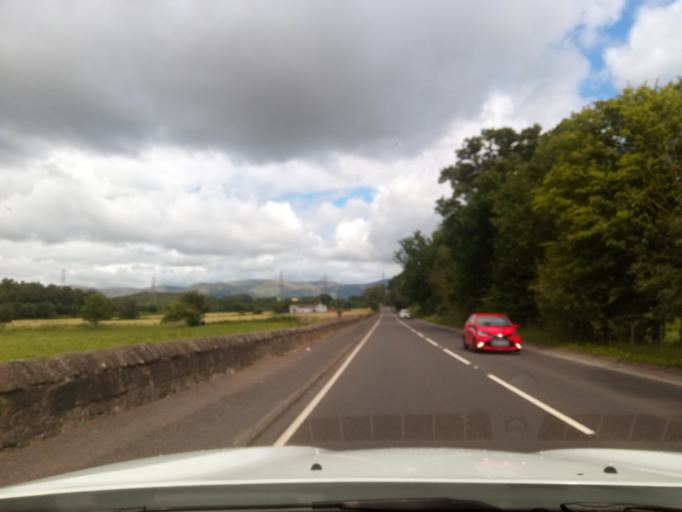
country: GB
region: Scotland
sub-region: Fife
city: Kincardine
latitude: 56.0806
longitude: -3.7202
